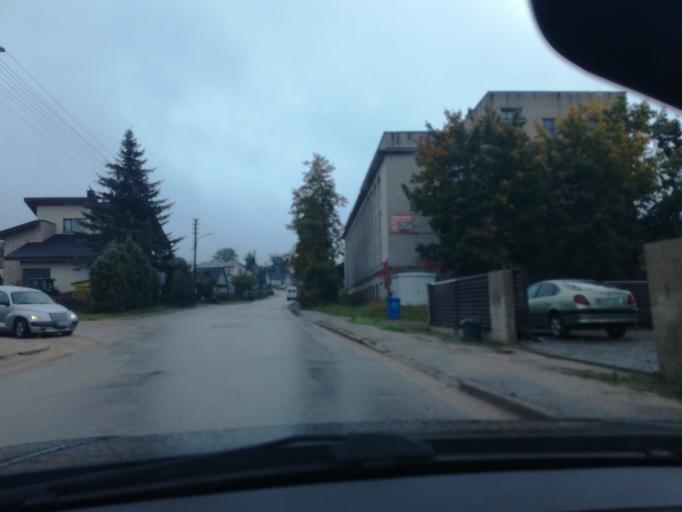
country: LT
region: Alytaus apskritis
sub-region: Alytus
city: Alytus
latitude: 54.4016
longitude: 24.0685
